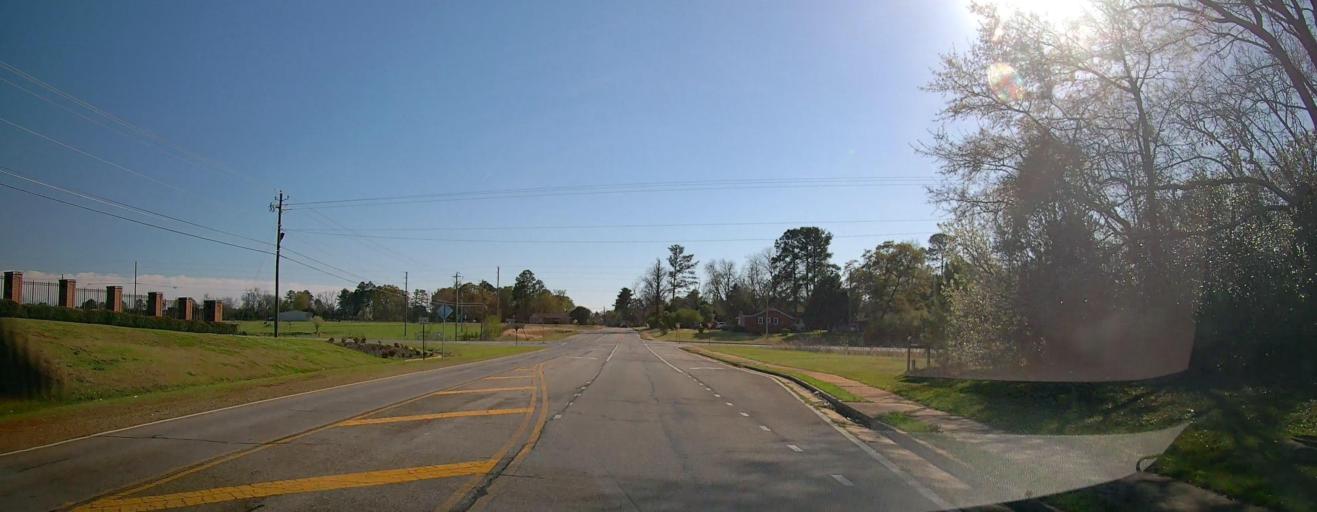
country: US
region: Georgia
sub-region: Peach County
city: Fort Valley
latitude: 32.5345
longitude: -83.9022
